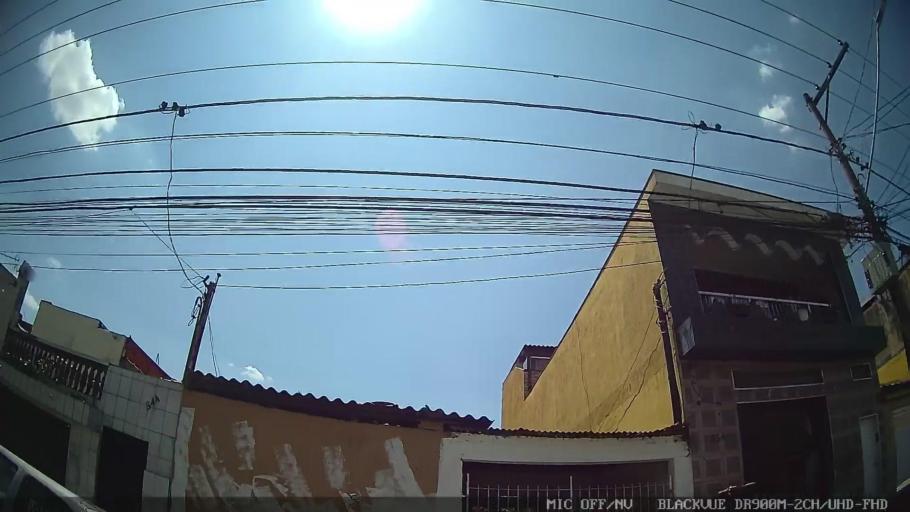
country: BR
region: Sao Paulo
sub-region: Guarulhos
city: Guarulhos
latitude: -23.5214
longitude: -46.4898
